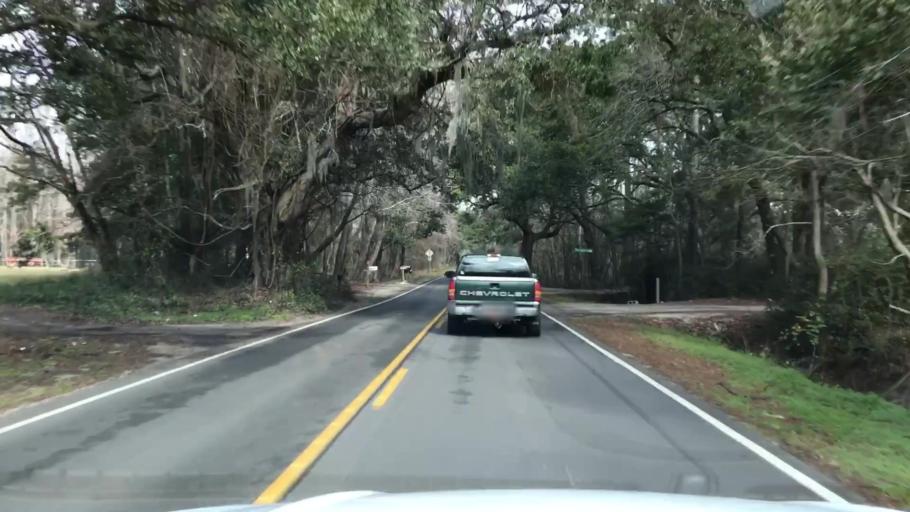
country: US
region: South Carolina
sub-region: Charleston County
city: Folly Beach
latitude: 32.6924
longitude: -80.0163
